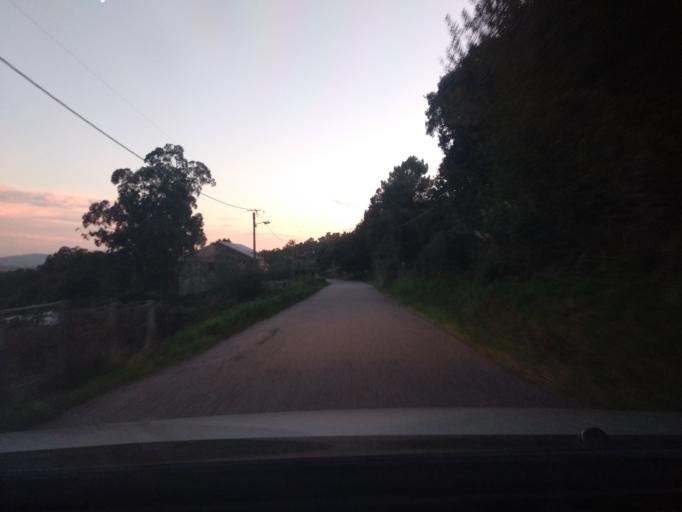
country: ES
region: Galicia
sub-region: Provincia de Pontevedra
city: Moana
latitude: 42.3051
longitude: -8.6989
